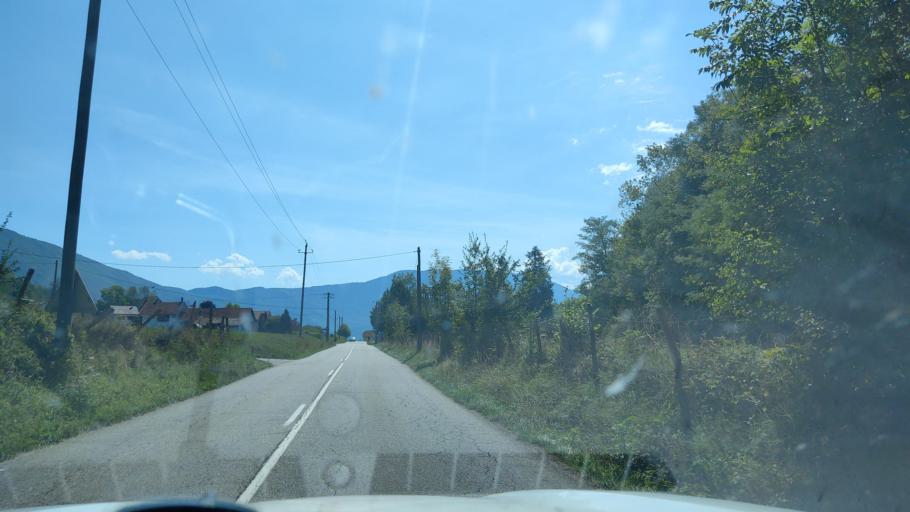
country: FR
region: Rhone-Alpes
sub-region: Departement de la Savoie
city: Novalaise
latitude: 45.5922
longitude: 5.7806
